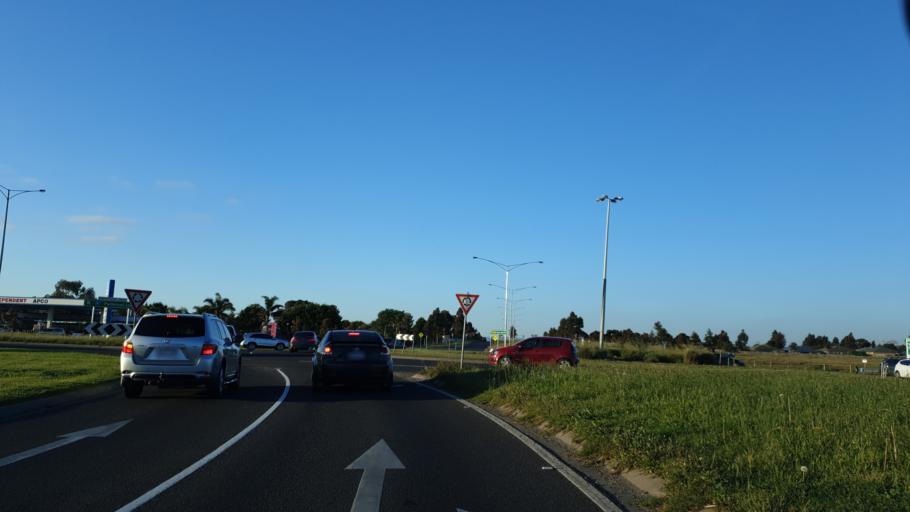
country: AU
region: Victoria
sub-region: Casey
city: Cranbourne North
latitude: -38.0852
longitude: 145.2954
